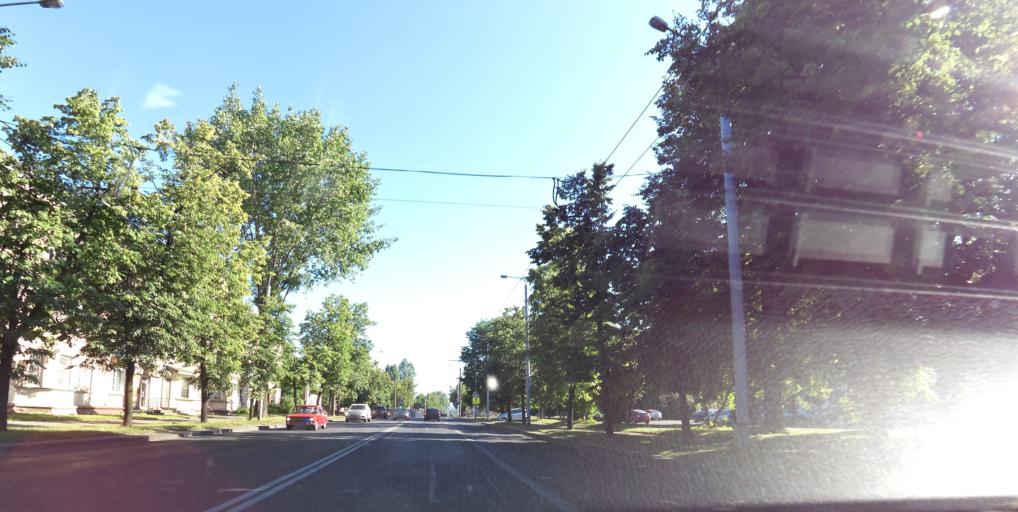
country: LT
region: Vilnius County
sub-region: Vilnius
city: Vilnius
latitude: 54.7100
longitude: 25.2860
